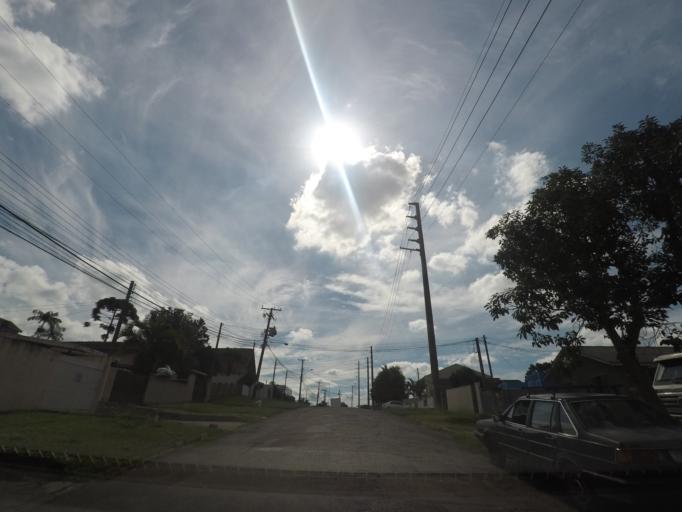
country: BR
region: Parana
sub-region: Curitiba
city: Curitiba
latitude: -25.4920
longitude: -49.2702
